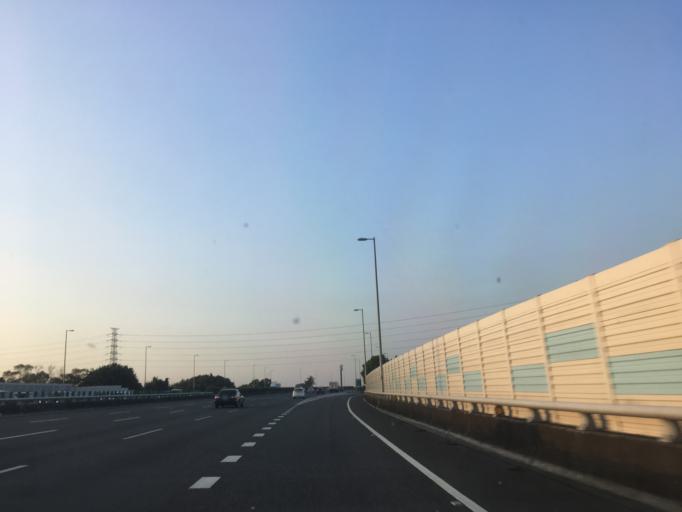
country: TW
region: Taiwan
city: Zhongxing New Village
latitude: 24.0011
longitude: 120.6505
